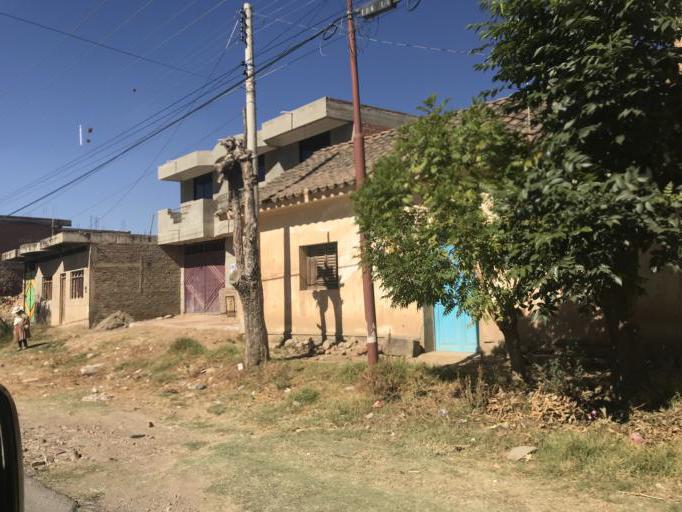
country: BO
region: Cochabamba
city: Cliza
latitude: -17.5778
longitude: -65.9076
